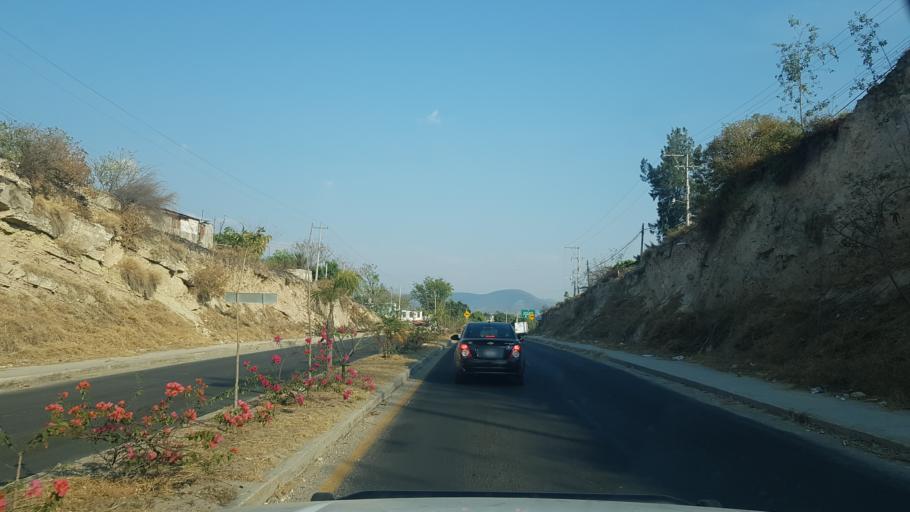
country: MX
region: Puebla
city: Izucar de Matamoros
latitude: 18.6036
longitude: -98.4833
